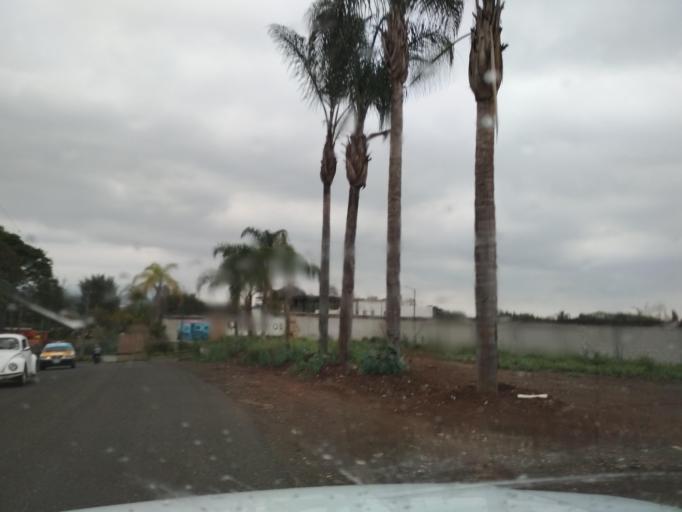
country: MX
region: Veracruz
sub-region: Cordoba
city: Veinte de Noviembre
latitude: 18.8717
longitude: -96.9518
